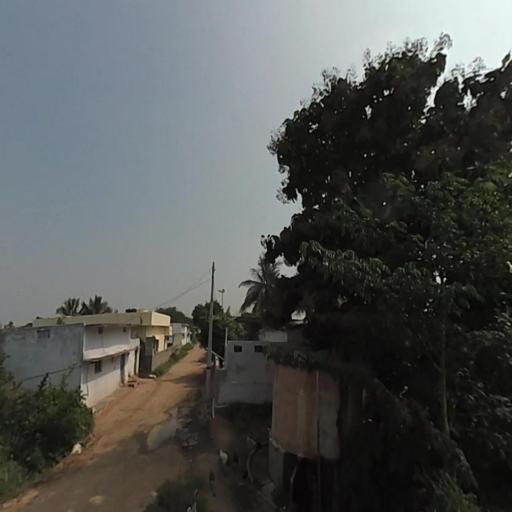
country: IN
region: Telangana
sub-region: Nalgonda
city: Nalgonda
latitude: 17.2042
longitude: 79.1468
